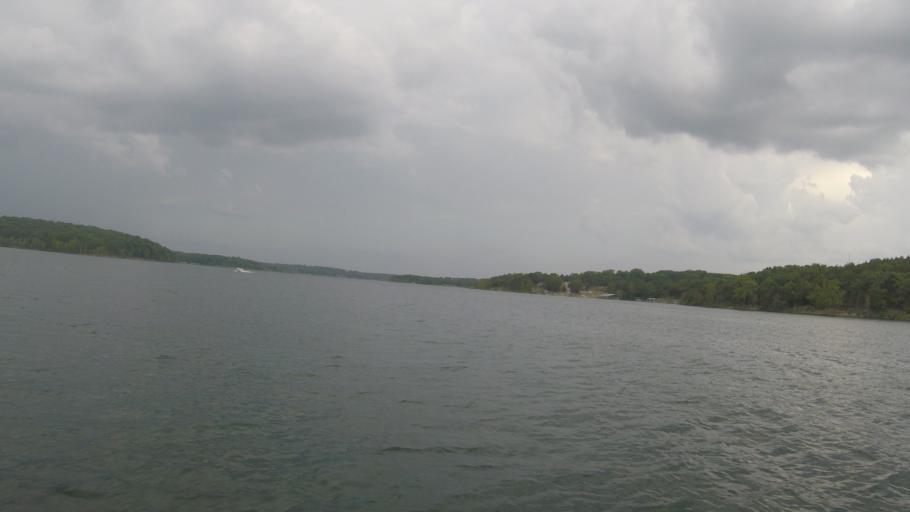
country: US
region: Missouri
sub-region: Barry County
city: Shell Knob
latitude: 36.5909
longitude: -93.5497
